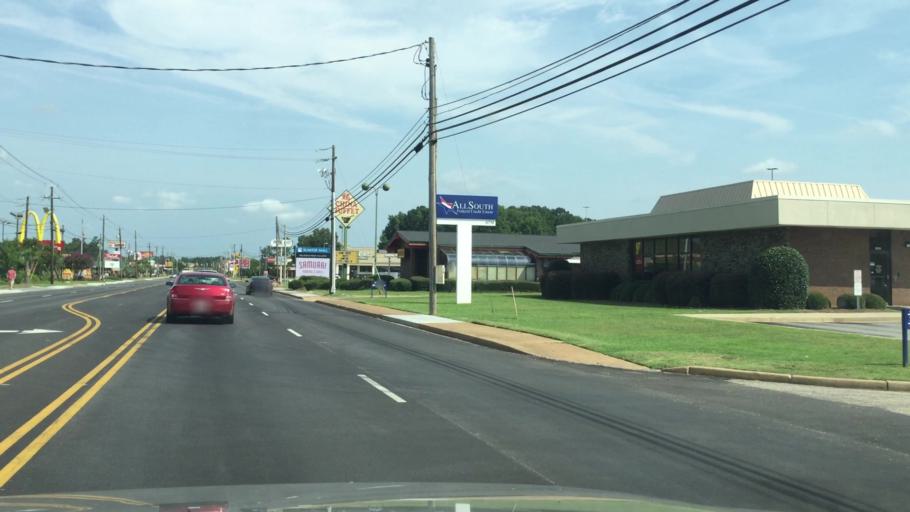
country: US
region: South Carolina
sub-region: Sumter County
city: Sumter
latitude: 33.9482
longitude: -80.3747
